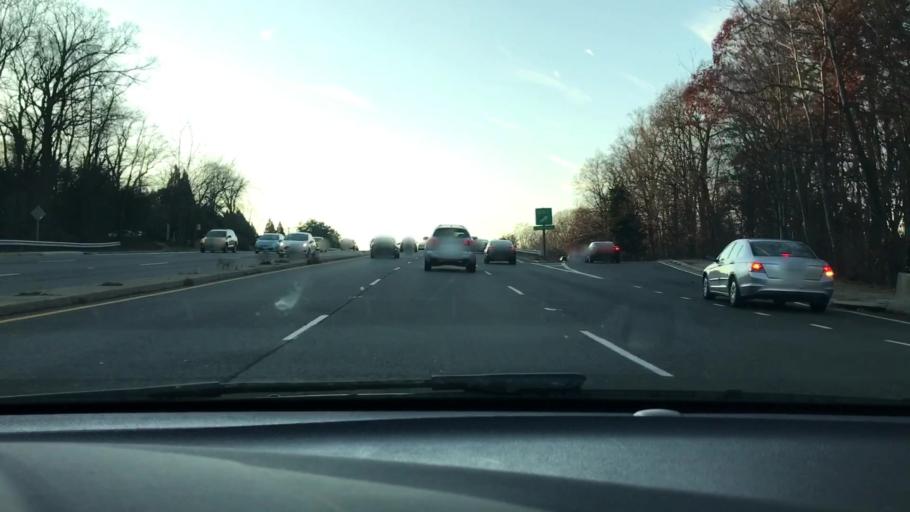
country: US
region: Virginia
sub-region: Fairfax County
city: Baileys Crossroads
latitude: 38.8665
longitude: -77.1254
